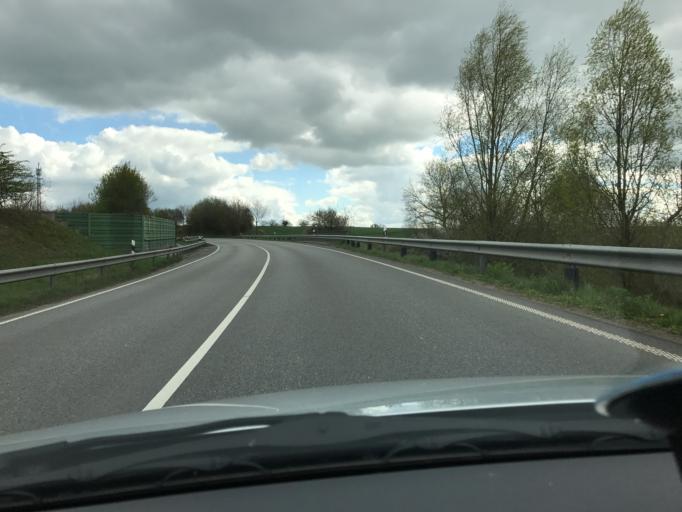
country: DE
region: Schleswig-Holstein
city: Eutin
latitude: 54.1243
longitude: 10.5814
